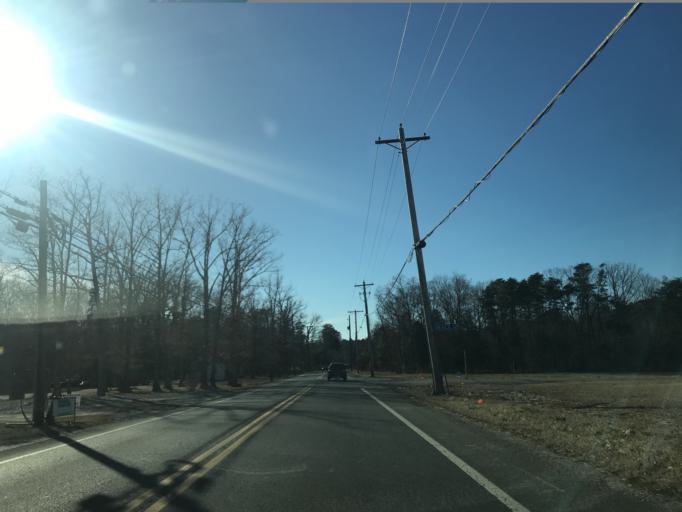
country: US
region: Maryland
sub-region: Charles County
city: Waldorf
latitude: 38.6862
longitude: -76.9140
